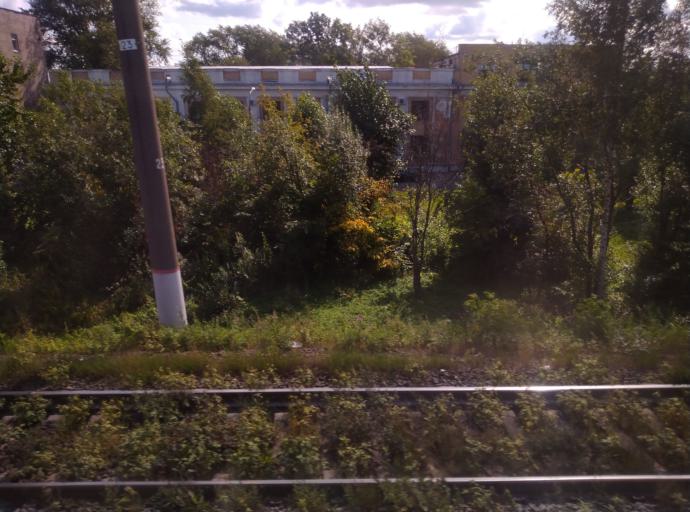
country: RU
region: St.-Petersburg
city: Centralniy
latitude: 59.9076
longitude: 30.3846
